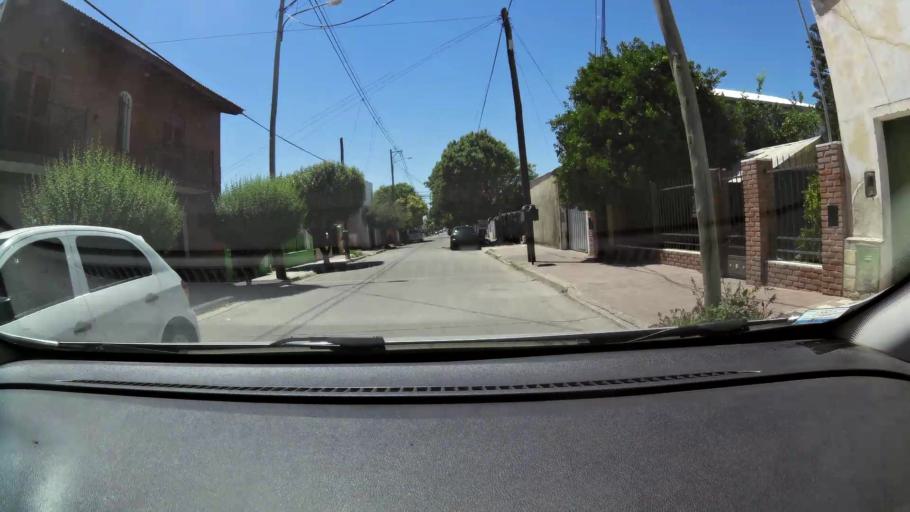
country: AR
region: Cordoba
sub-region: Departamento de Capital
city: Cordoba
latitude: -31.4286
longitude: -64.1190
